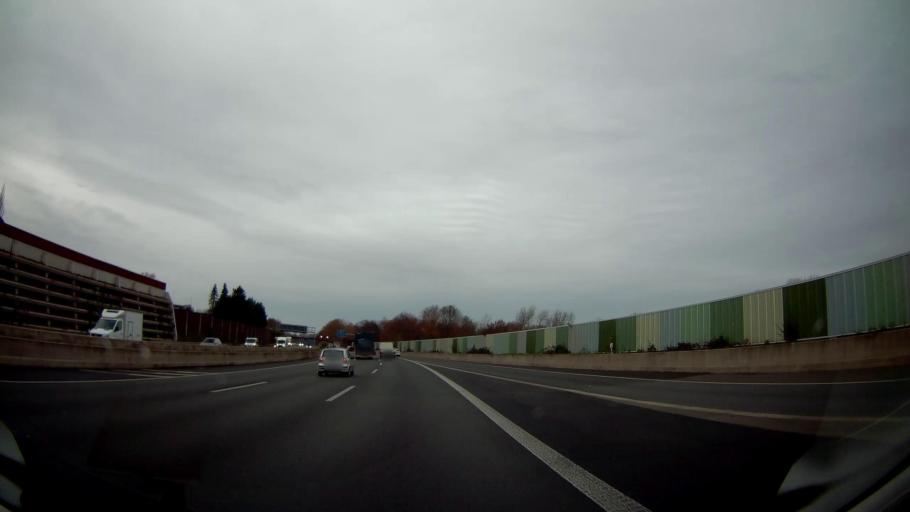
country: DE
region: North Rhine-Westphalia
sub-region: Regierungsbezirk Munster
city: Gelsenkirchen
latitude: 51.4719
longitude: 7.0990
